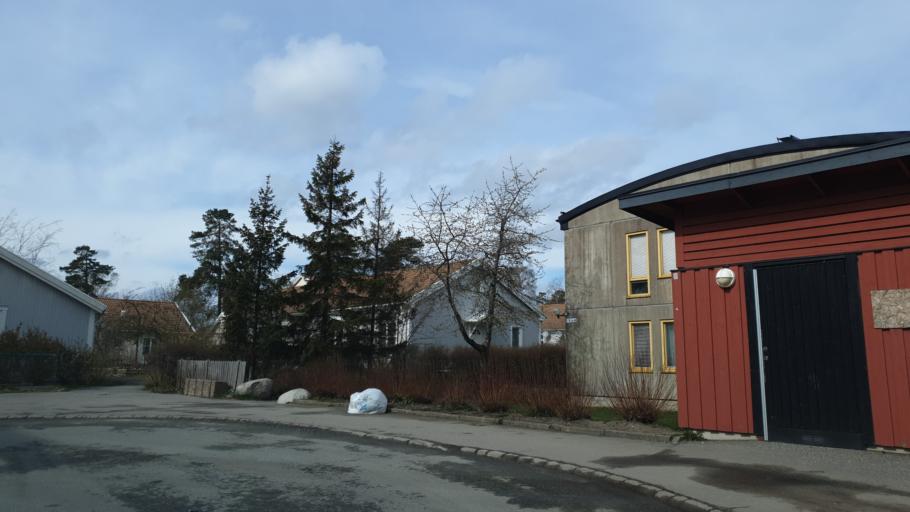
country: SE
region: Stockholm
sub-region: Nacka Kommun
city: Boo
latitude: 59.3278
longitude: 18.2549
